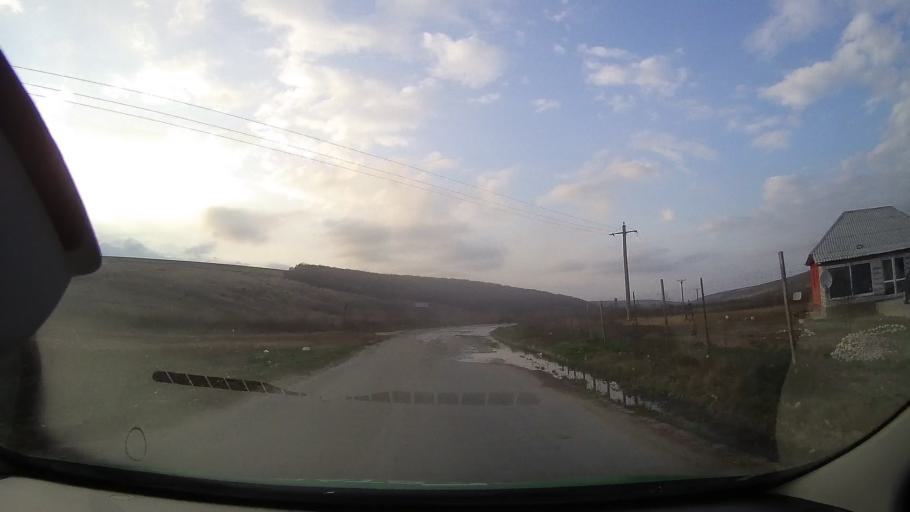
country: RO
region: Constanta
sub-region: Comuna Dobromir
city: Dobromir
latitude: 44.0217
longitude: 27.8714
